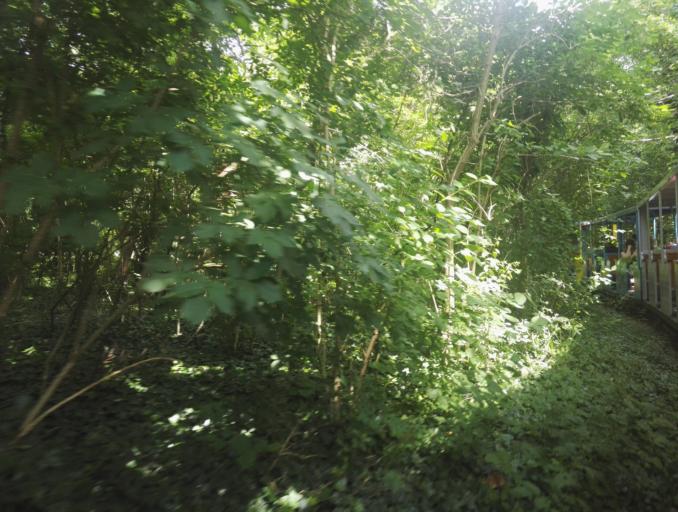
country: AT
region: Vienna
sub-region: Wien Stadt
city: Vienna
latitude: 48.2360
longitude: 16.4100
